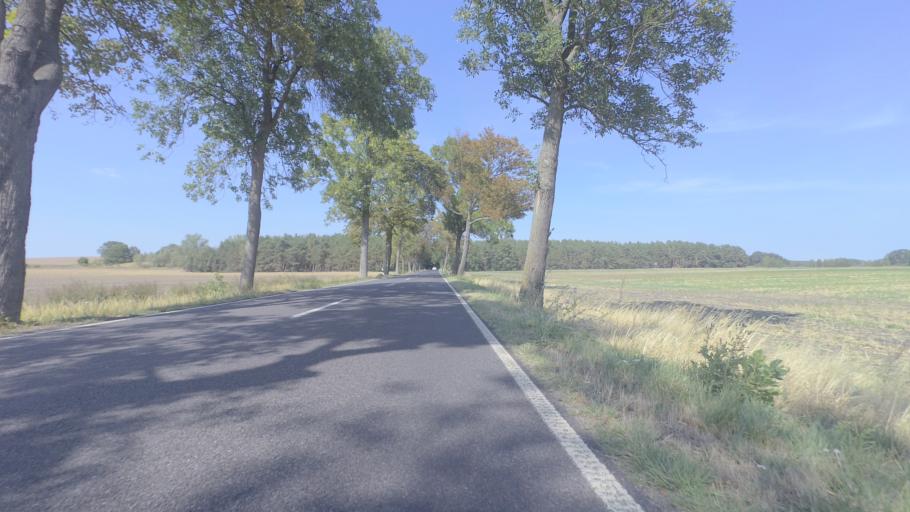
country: DE
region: Brandenburg
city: Am Mellensee
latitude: 52.2045
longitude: 13.3958
